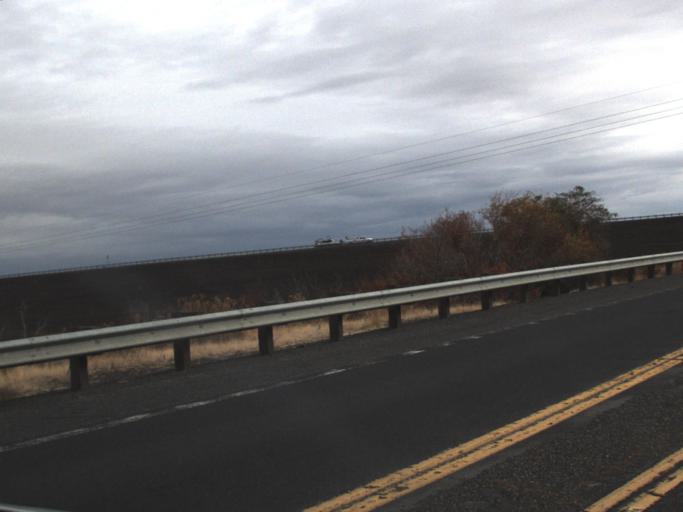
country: US
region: Washington
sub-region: Asotin County
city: Clarkston
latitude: 46.4742
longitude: -117.0408
